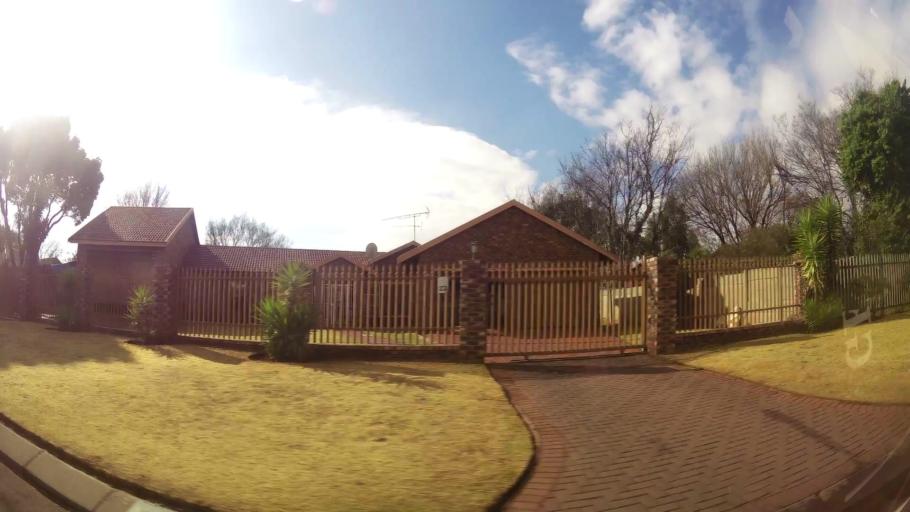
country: ZA
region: Gauteng
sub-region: Sedibeng District Municipality
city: Meyerton
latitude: -26.5519
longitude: 28.0354
